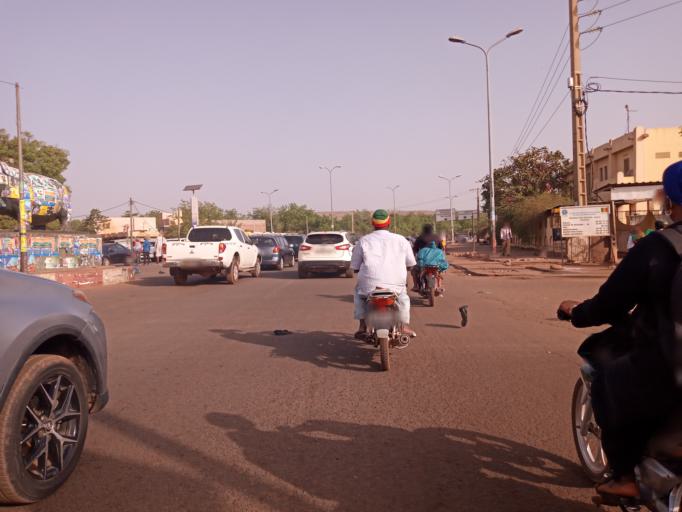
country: ML
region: Bamako
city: Bamako
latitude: 12.6452
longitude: -8.0092
